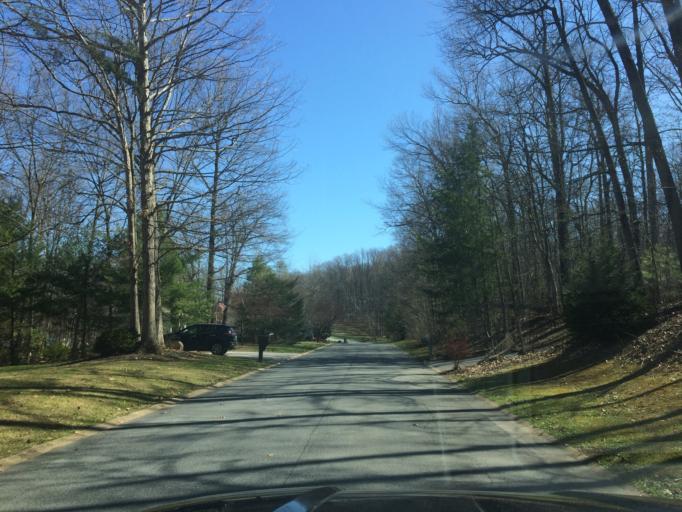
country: US
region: Pennsylvania
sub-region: York County
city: Parkville
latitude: 39.7002
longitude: -76.9764
